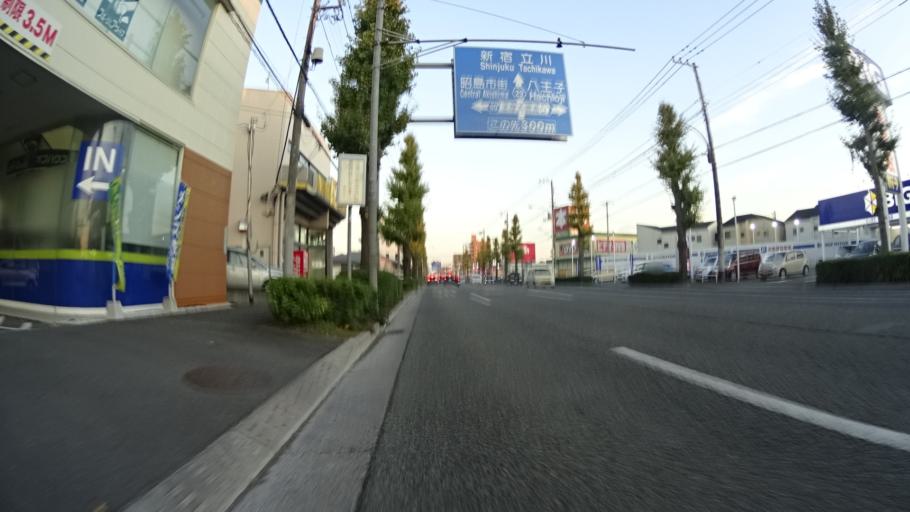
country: JP
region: Tokyo
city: Hino
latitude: 35.6979
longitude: 139.3727
